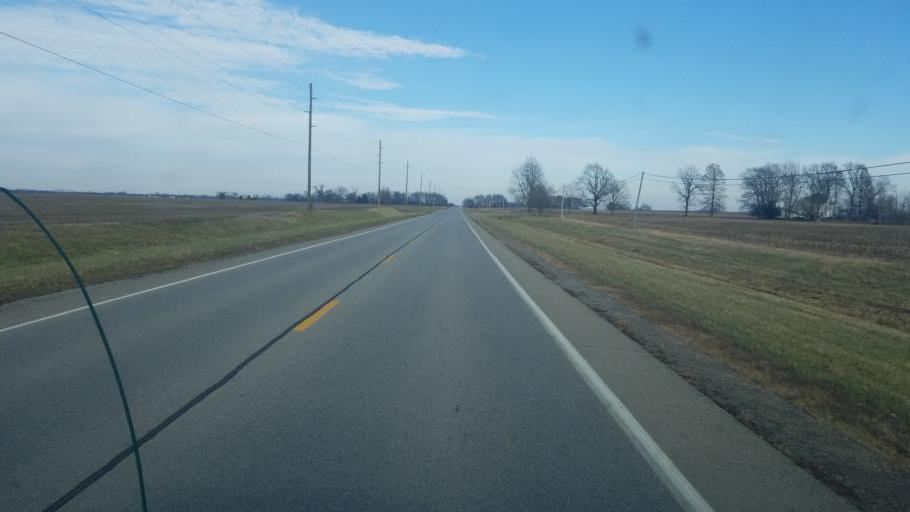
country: US
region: Illinois
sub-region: White County
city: Carmi
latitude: 38.1123
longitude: -88.1196
